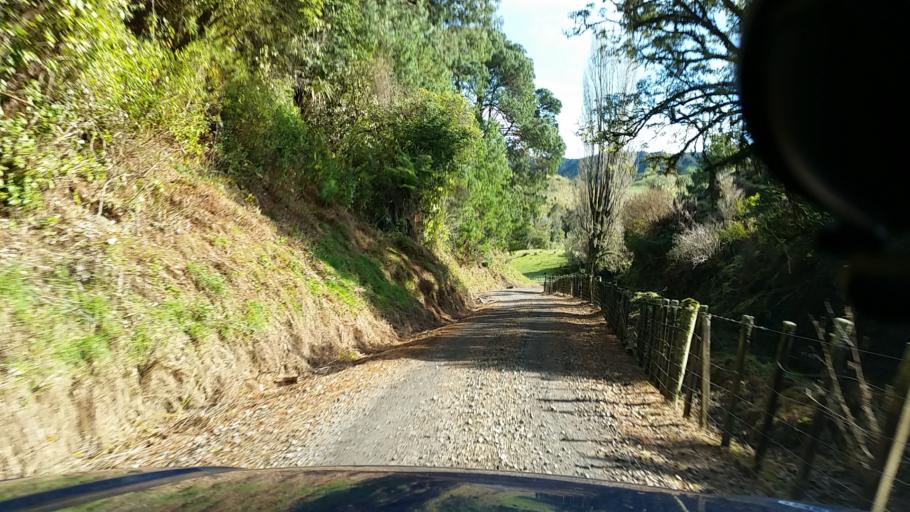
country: NZ
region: Taranaki
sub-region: New Plymouth District
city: Waitara
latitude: -39.0349
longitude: 174.7811
